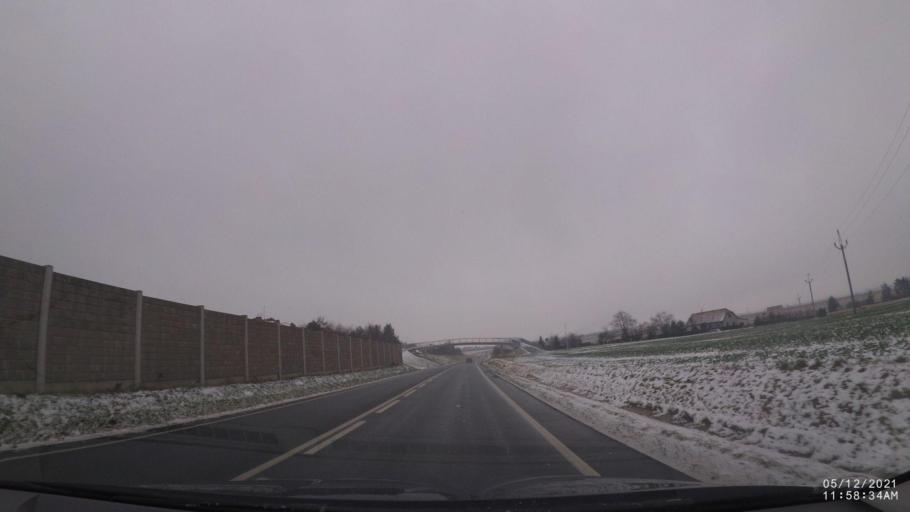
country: CZ
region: Kralovehradecky
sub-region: Okres Rychnov nad Kneznou
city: Opocno
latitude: 50.2737
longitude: 16.1153
